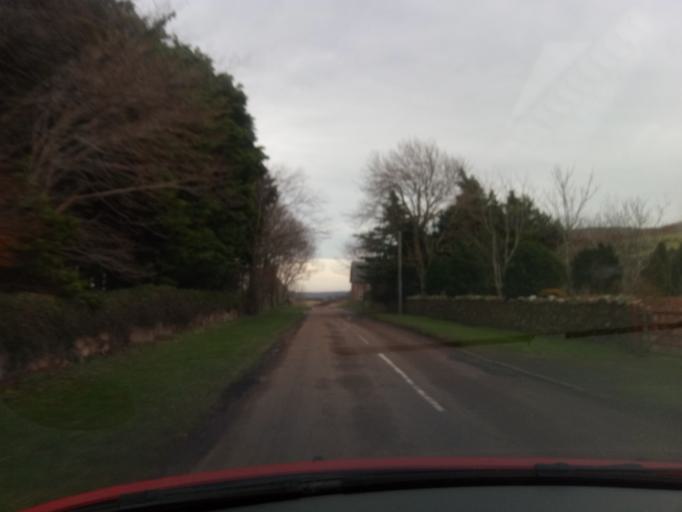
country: GB
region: England
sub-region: Northumberland
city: Kirknewton
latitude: 55.5663
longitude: -2.1031
